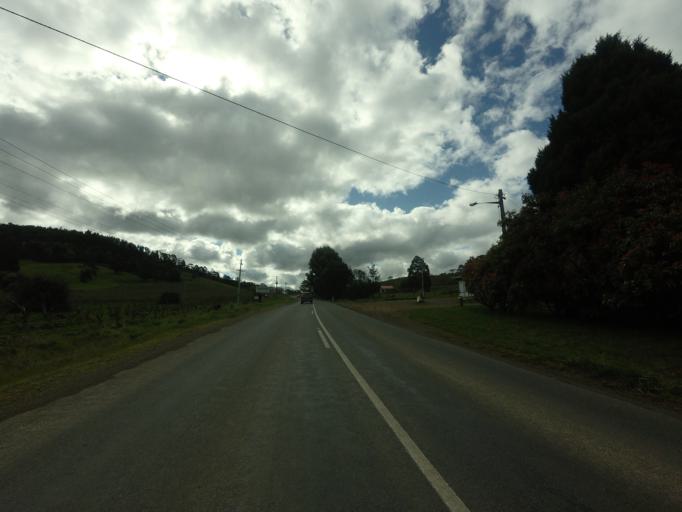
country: AU
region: Tasmania
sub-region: Huon Valley
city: Geeveston
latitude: -43.1882
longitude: 146.9581
